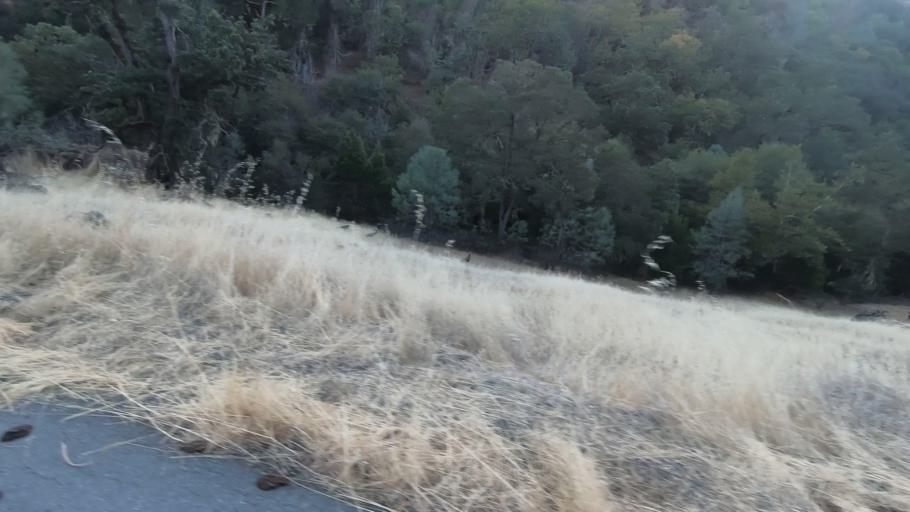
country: US
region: California
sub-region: Santa Clara County
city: East Foothills
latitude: 37.3695
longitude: -121.6708
